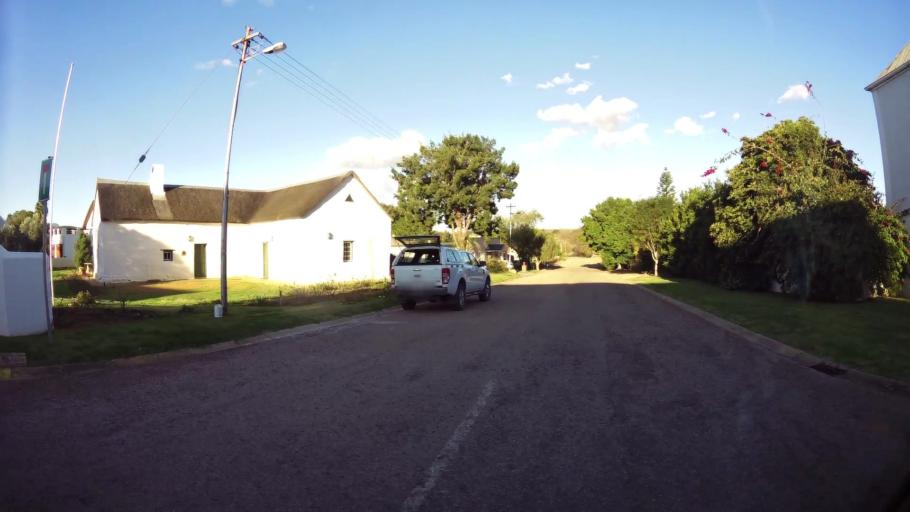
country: ZA
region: Western Cape
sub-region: Eden District Municipality
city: Riversdale
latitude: -34.0881
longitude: 20.9605
